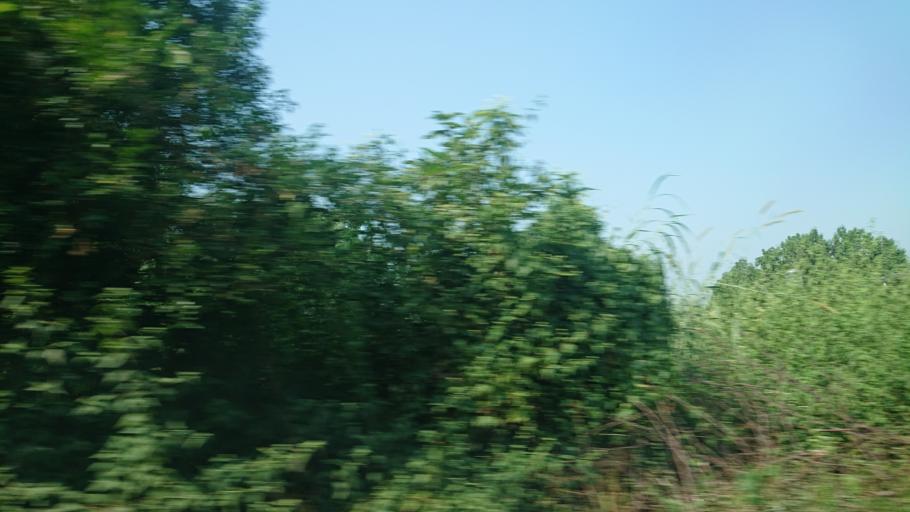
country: TW
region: Taiwan
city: Lugu
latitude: 23.6978
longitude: 120.6630
